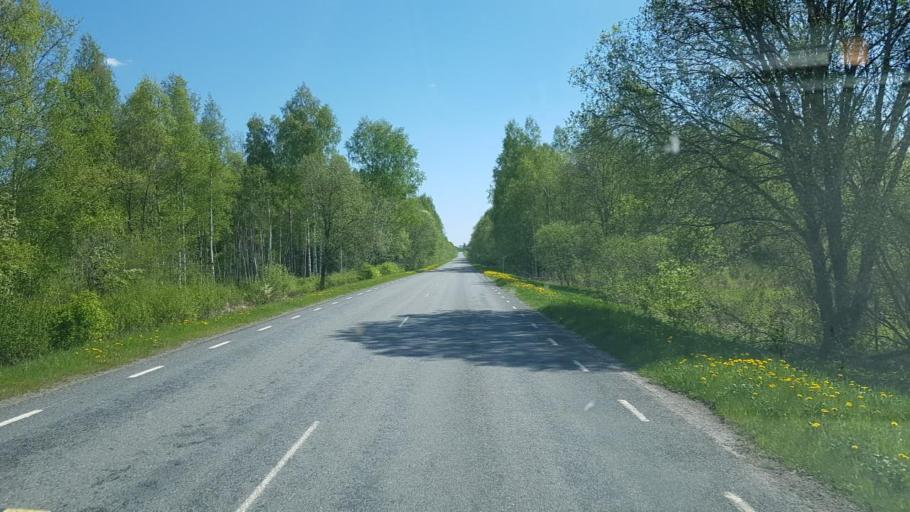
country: EE
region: Harju
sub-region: Raasiku vald
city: Raasiku
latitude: 59.3803
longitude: 25.2433
